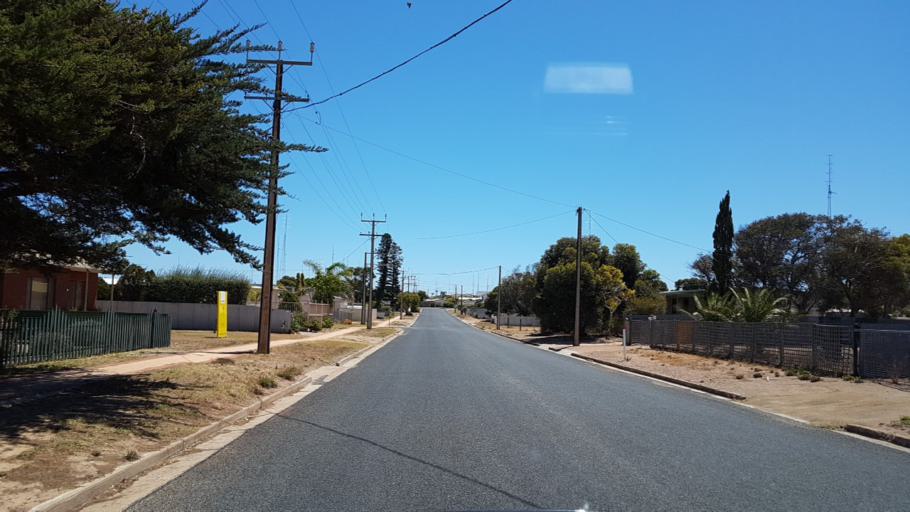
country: AU
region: South Australia
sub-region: Copper Coast
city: Wallaroo
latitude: -33.8991
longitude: 137.6303
